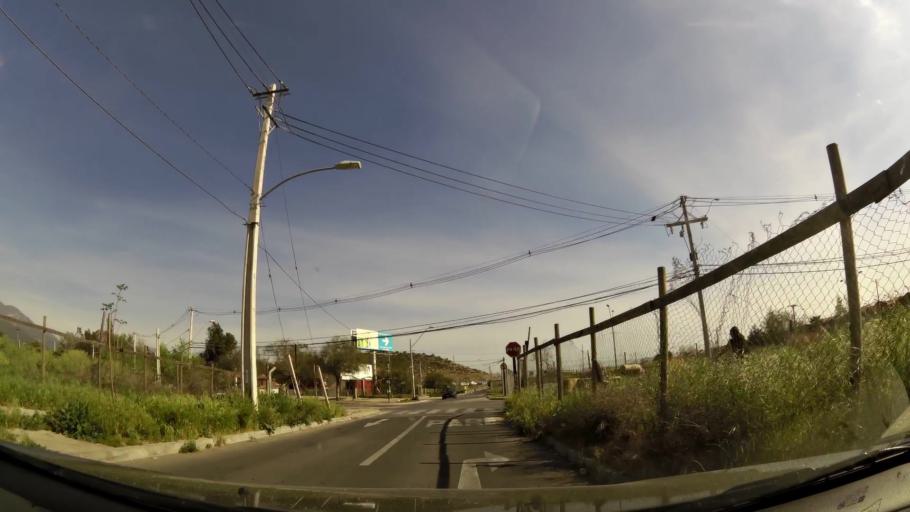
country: CL
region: Santiago Metropolitan
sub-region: Provincia de Cordillera
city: Puente Alto
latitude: -33.5925
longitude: -70.5524
